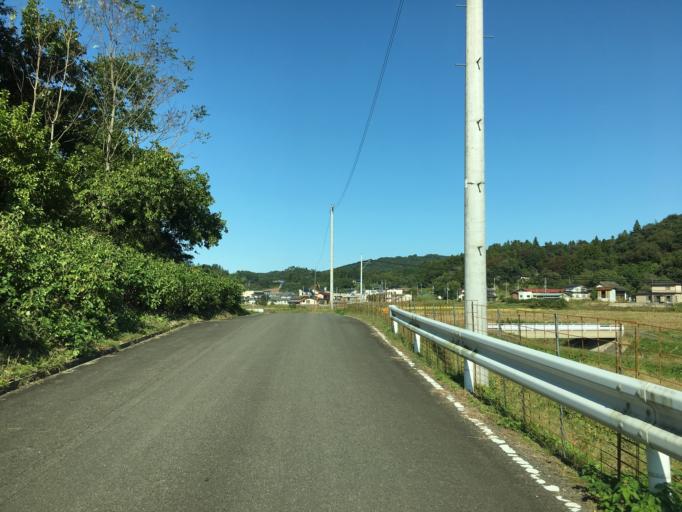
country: JP
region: Fukushima
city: Fukushima-shi
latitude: 37.6773
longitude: 140.5625
